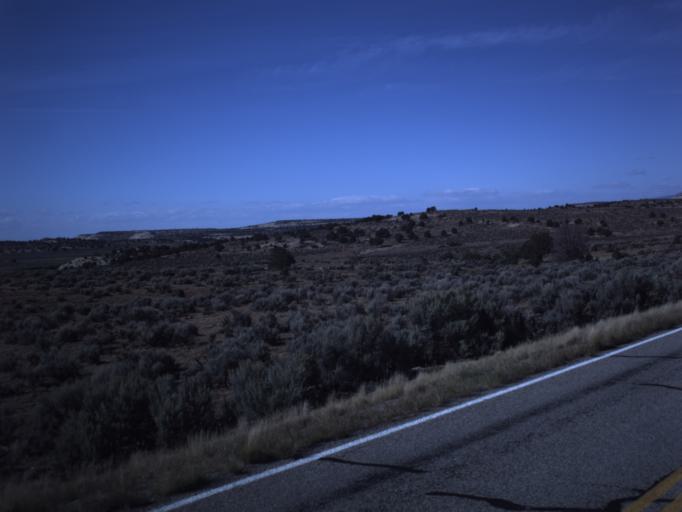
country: US
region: Utah
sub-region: San Juan County
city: Monticello
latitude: 38.0238
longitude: -109.4259
